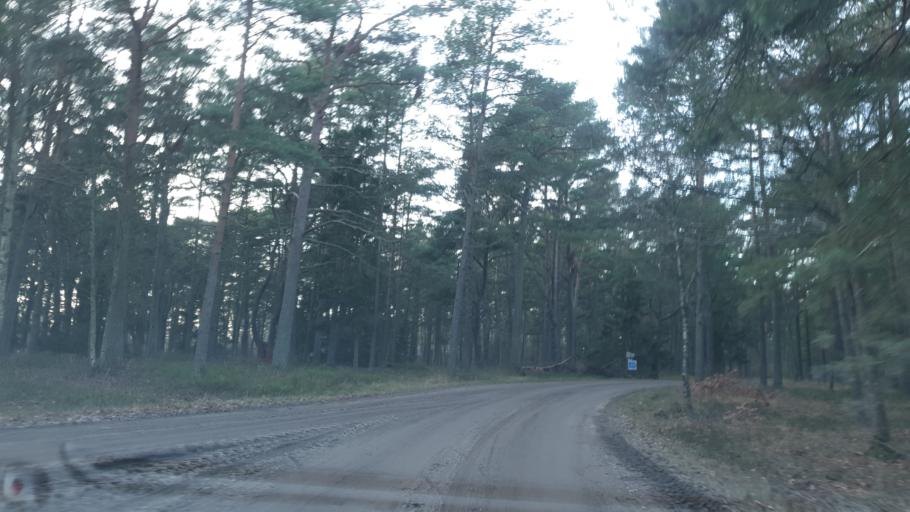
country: SE
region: Kalmar
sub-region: Torsas Kommun
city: Torsas
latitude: 56.3010
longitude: 16.0342
